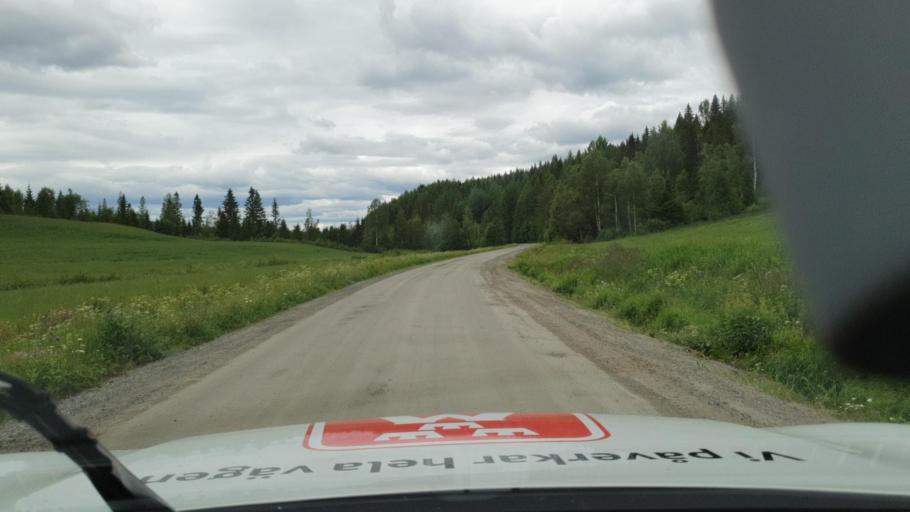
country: SE
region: Vaesterbotten
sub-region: Nordmalings Kommun
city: Nordmaling
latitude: 63.6836
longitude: 19.4517
